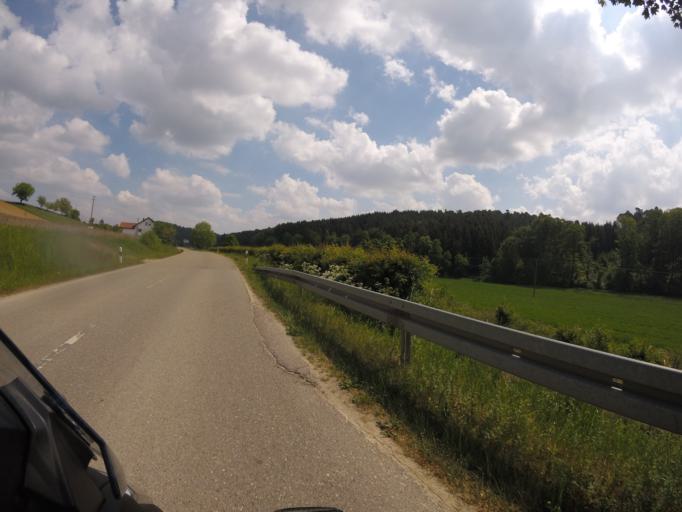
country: DE
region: Bavaria
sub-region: Upper Bavaria
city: Wolnzach
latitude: 48.5964
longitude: 11.6691
